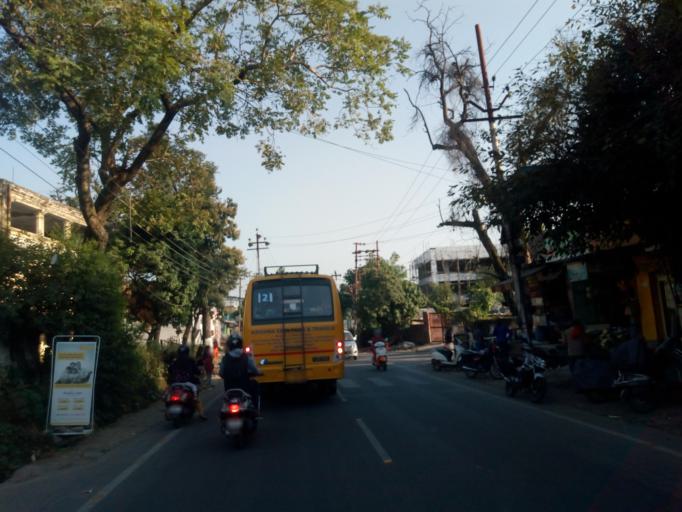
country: IN
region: Uttarakhand
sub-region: Dehradun
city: Dehradun
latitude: 30.3405
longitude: 78.0509
